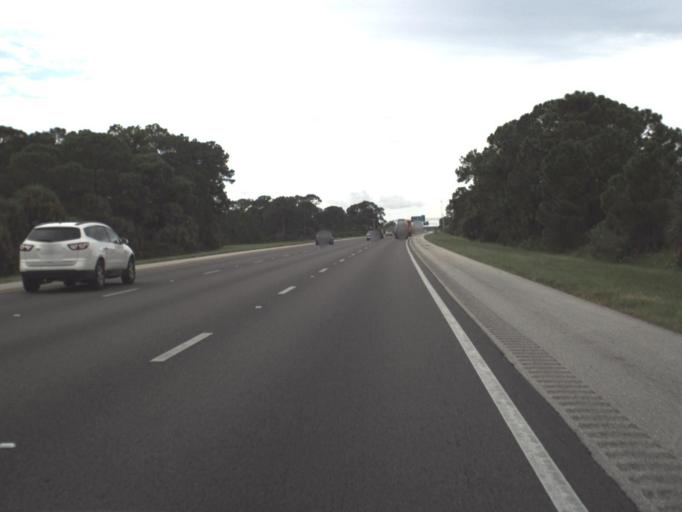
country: US
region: Florida
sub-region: Sarasota County
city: Osprey
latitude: 27.2051
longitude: -82.4426
